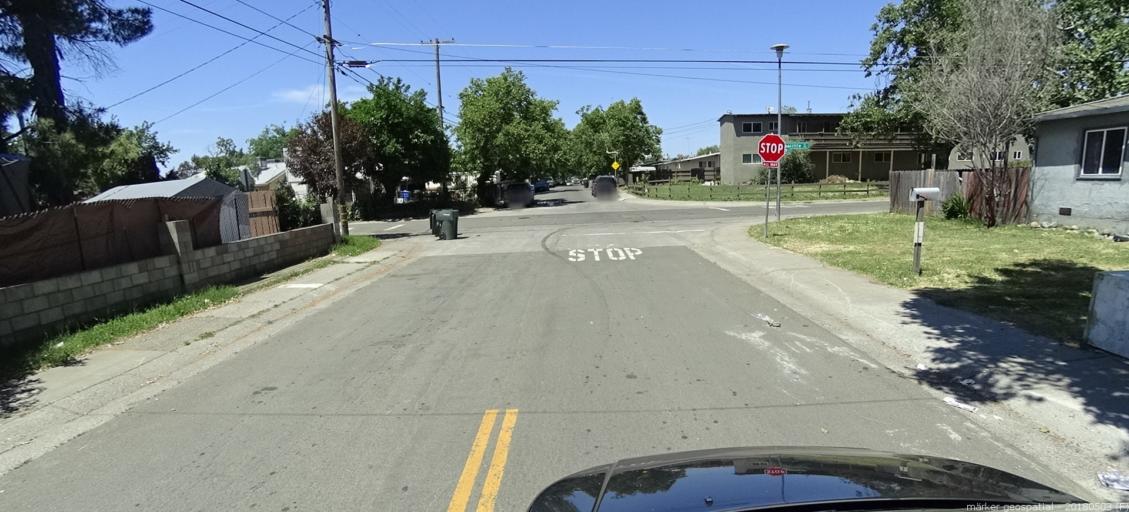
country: US
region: California
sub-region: Sacramento County
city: Rio Linda
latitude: 38.6426
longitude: -121.4255
